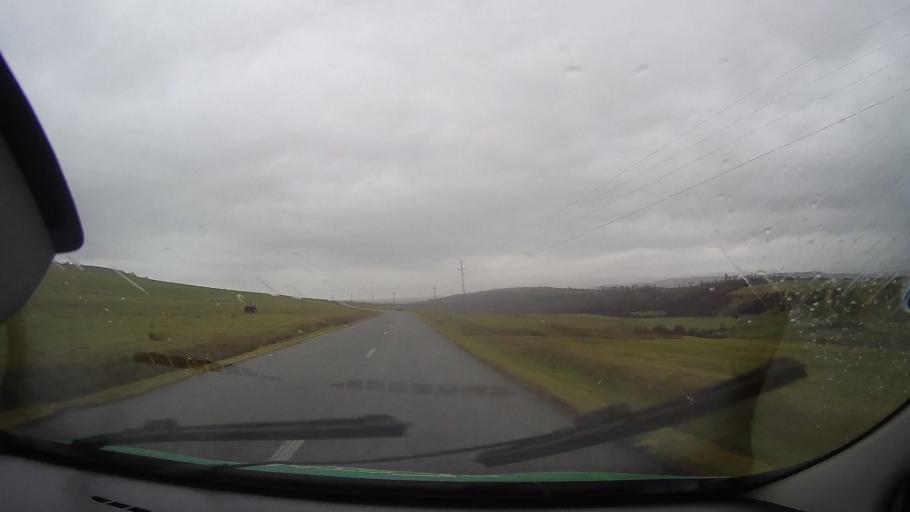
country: RO
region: Mures
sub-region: Comuna Brancovenesti
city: Valenii de Mures
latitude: 46.9107
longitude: 24.7832
